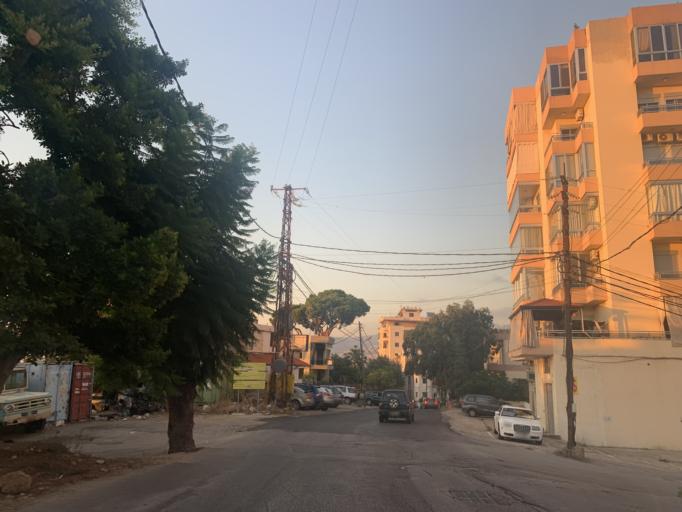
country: LB
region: Mont-Liban
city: Djounie
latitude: 33.9724
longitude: 35.6268
